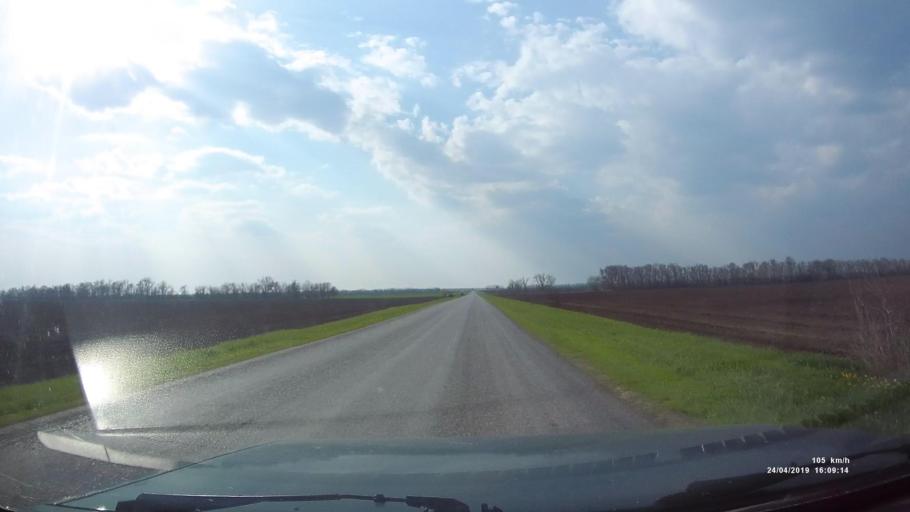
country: RU
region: Rostov
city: Sovetskoye
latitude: 46.7061
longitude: 42.2935
